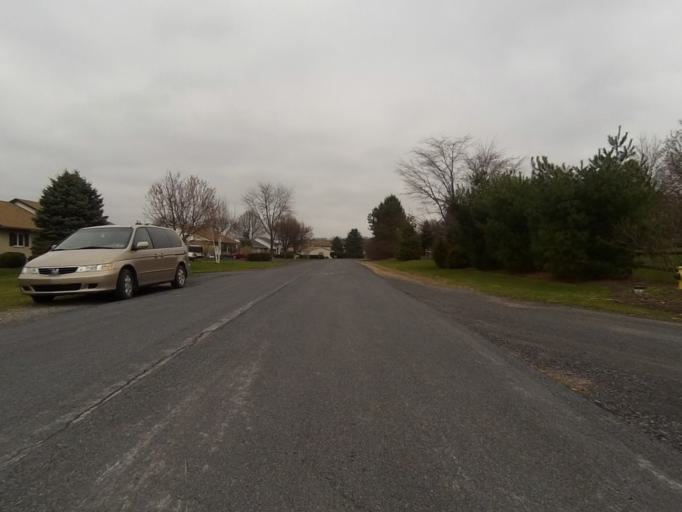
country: US
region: Pennsylvania
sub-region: Centre County
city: Boalsburg
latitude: 40.7875
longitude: -77.7784
